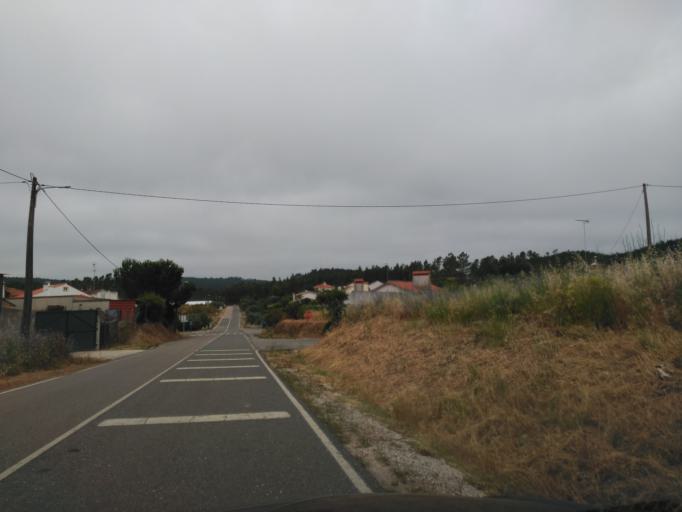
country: PT
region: Santarem
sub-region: Abrantes
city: Alferrarede
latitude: 39.5704
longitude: -8.1198
